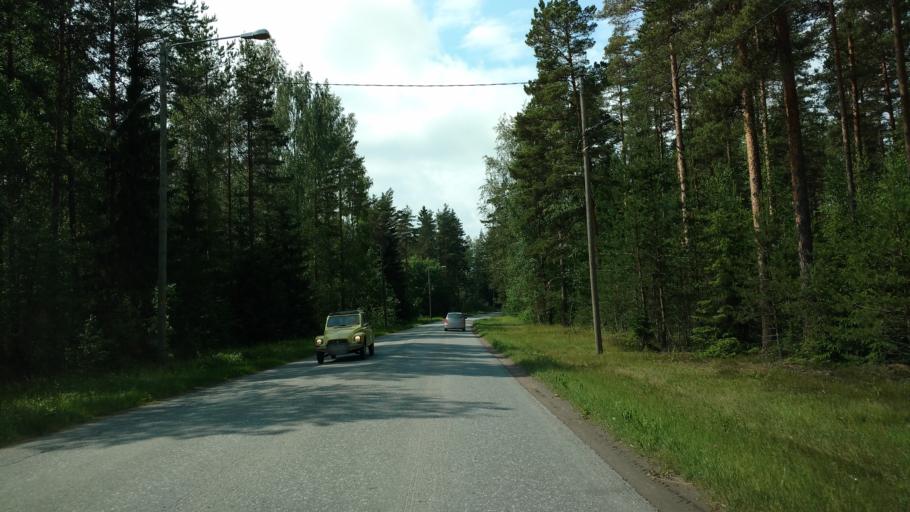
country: FI
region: Haeme
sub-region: Forssa
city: Ypaejae
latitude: 60.8054
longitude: 23.3103
